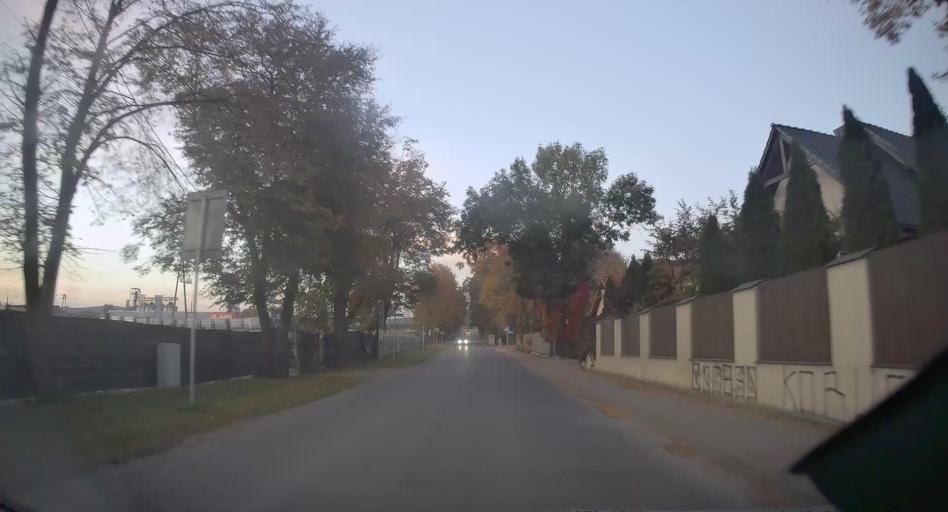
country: PL
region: Lesser Poland Voivodeship
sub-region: Powiat krakowski
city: Zabierzow
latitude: 50.1250
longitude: 19.8218
